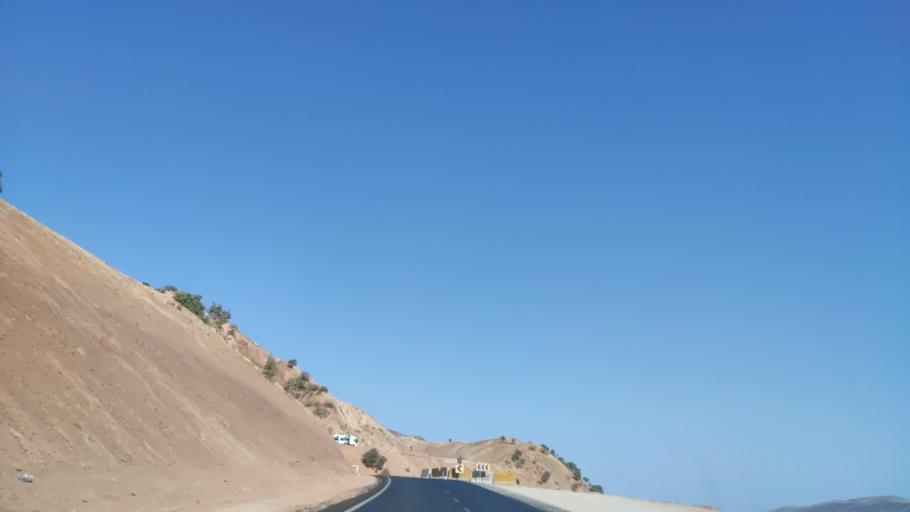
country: IQ
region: Arbil
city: Shaqlawah
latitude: 36.4336
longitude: 44.3028
